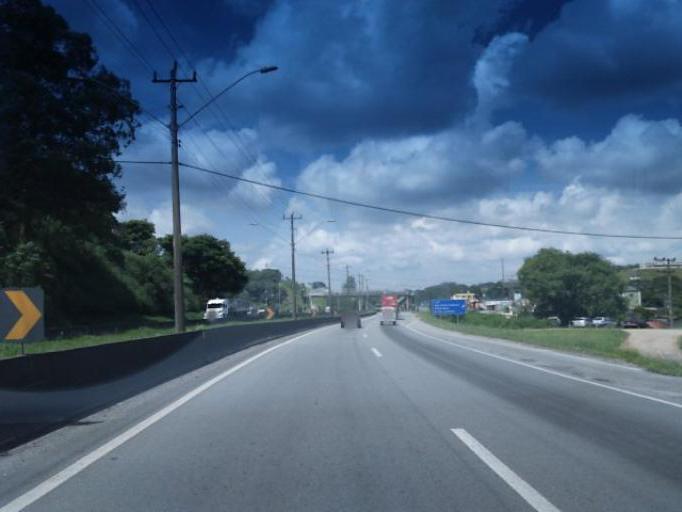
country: BR
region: Sao Paulo
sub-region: Itapecerica Da Serra
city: Itapecerica da Serra
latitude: -23.7192
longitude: -46.8835
